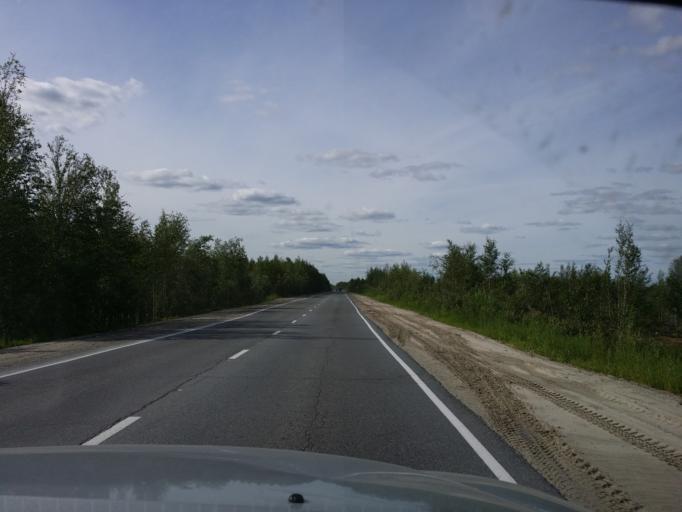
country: RU
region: Khanty-Mansiyskiy Avtonomnyy Okrug
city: Nizhnevartovsk
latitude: 61.1096
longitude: 76.6095
